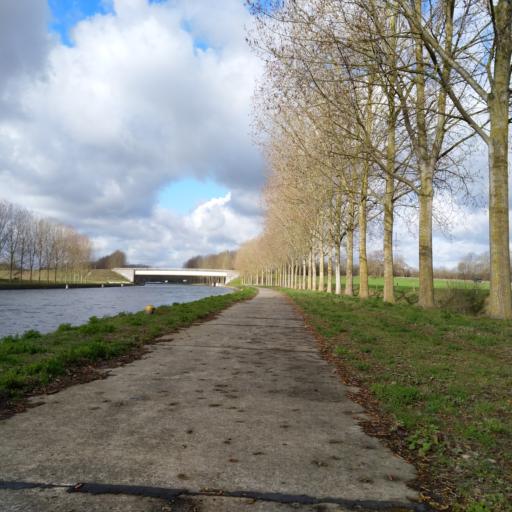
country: BE
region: Wallonia
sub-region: Province du Hainaut
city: Mons
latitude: 50.4834
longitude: 3.9705
